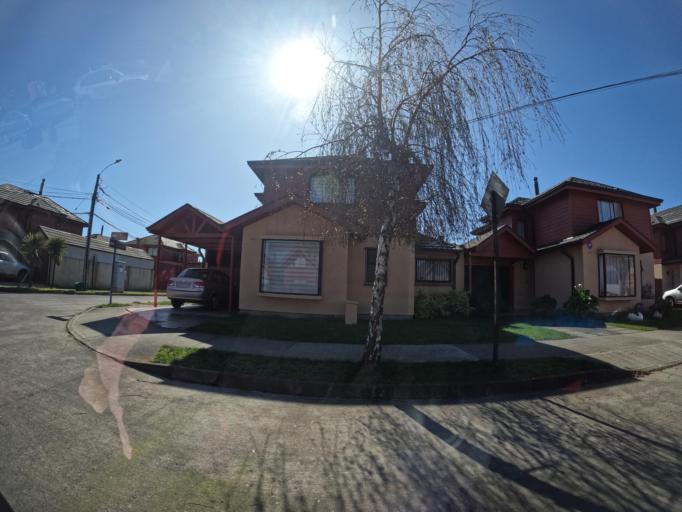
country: CL
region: Biobio
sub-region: Provincia de Concepcion
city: Concepcion
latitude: -36.8880
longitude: -73.1447
